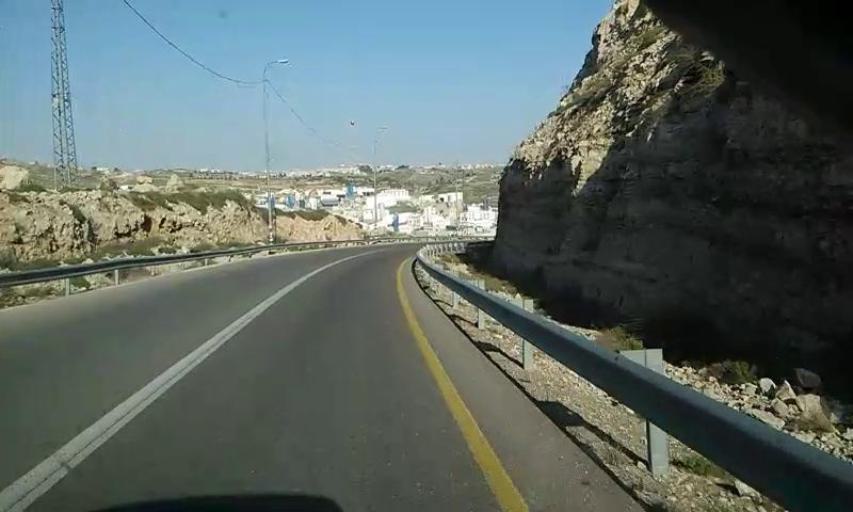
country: PS
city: Khallat ad Dar
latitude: 31.5005
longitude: 35.1150
